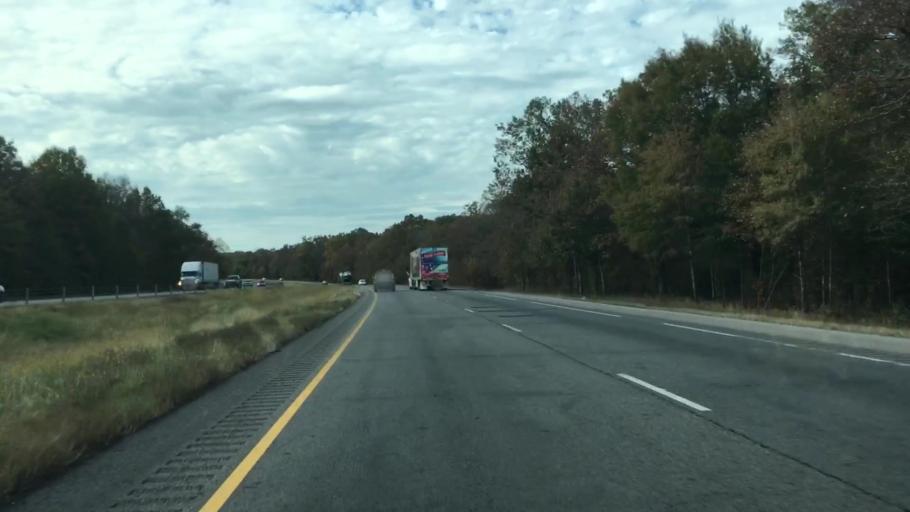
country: US
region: Arkansas
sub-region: Pope County
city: Atkins
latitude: 35.2445
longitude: -92.8636
